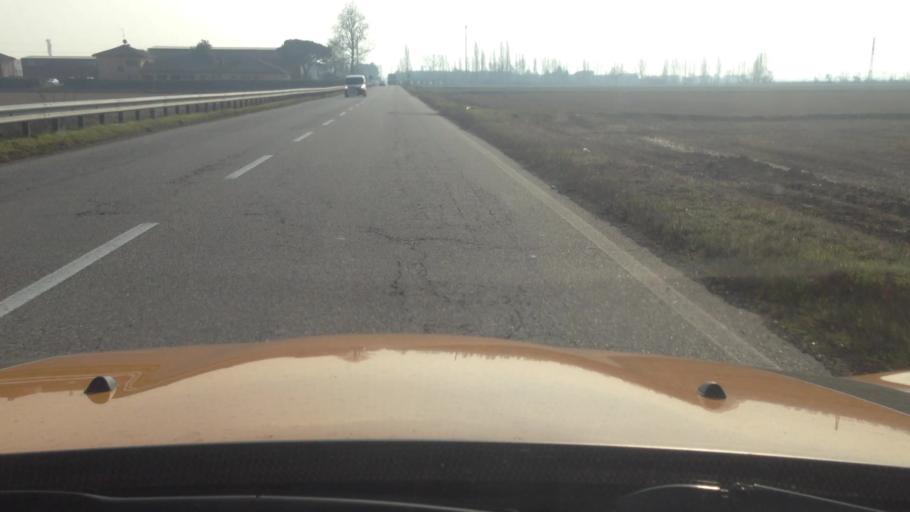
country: IT
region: Piedmont
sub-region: Provincia di Novara
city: San Pietro Mosezzo
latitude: 45.4657
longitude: 8.5579
